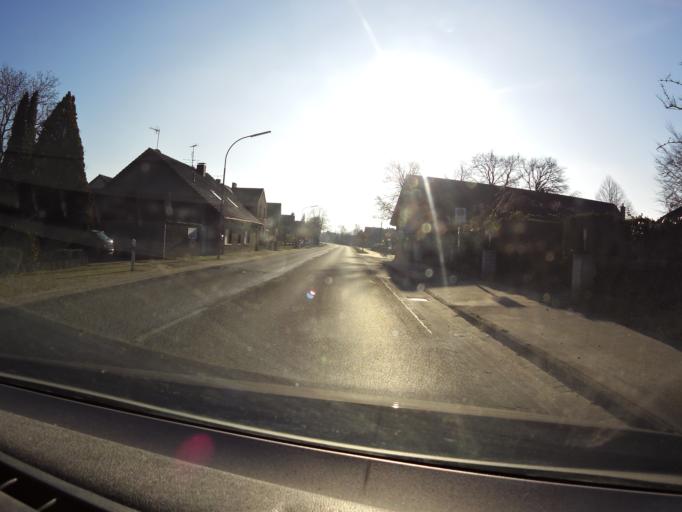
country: DE
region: North Rhine-Westphalia
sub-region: Regierungsbezirk Dusseldorf
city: Bruggen
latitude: 51.2564
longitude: 6.1839
